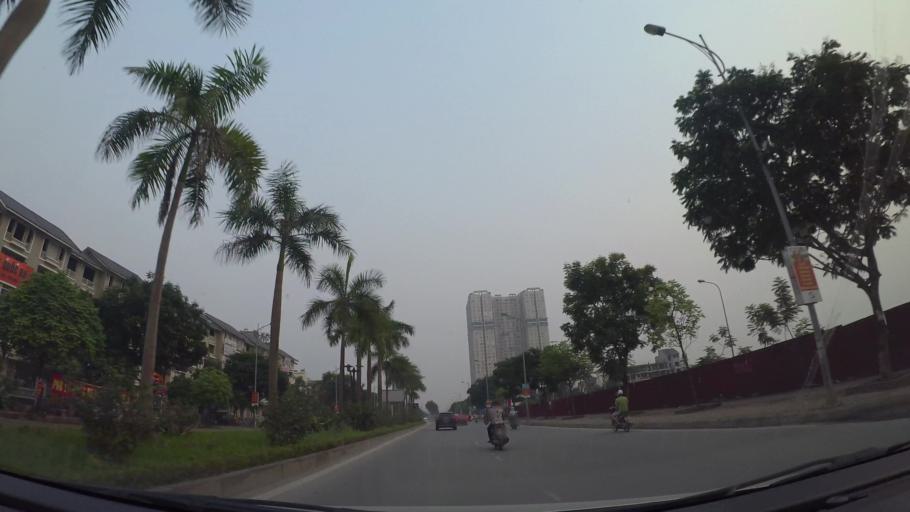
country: VN
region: Ha Noi
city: Cau Dien
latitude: 21.0069
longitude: 105.7316
